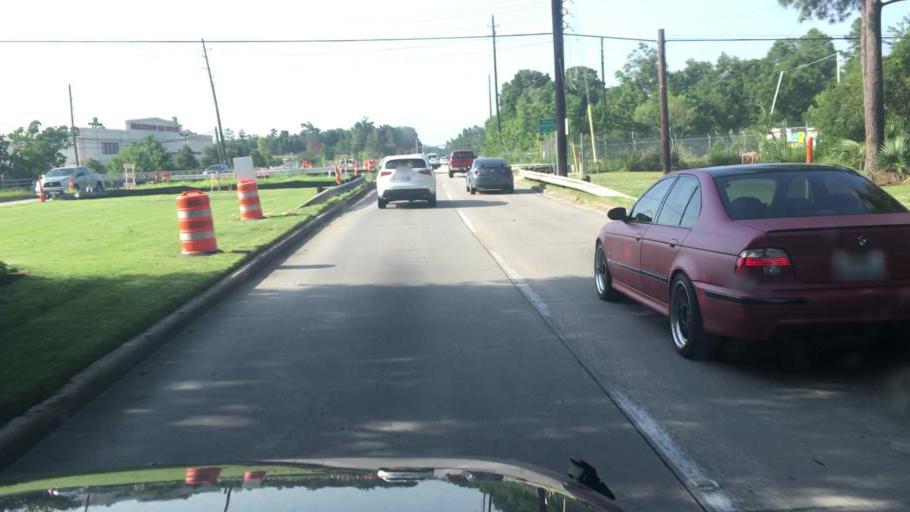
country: US
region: Texas
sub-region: Harris County
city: Atascocita
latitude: 29.9344
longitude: -95.1762
